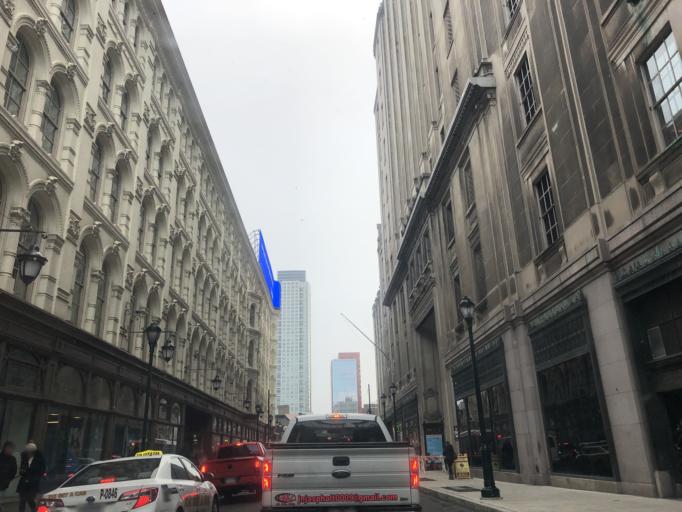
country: US
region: Pennsylvania
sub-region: Philadelphia County
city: Philadelphia
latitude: 39.9520
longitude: -75.1533
